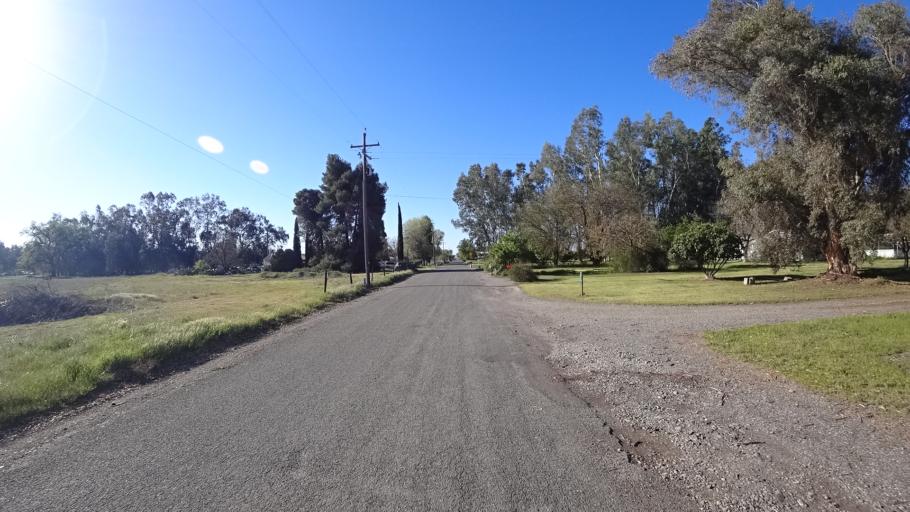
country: US
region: California
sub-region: Glenn County
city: Orland
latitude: 39.7690
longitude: -122.2202
